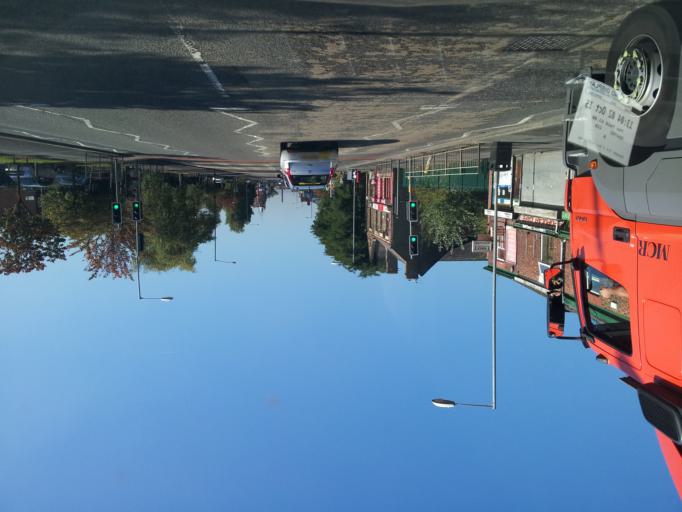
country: GB
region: England
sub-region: Manchester
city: Failsworth
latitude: 53.5020
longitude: -2.1895
